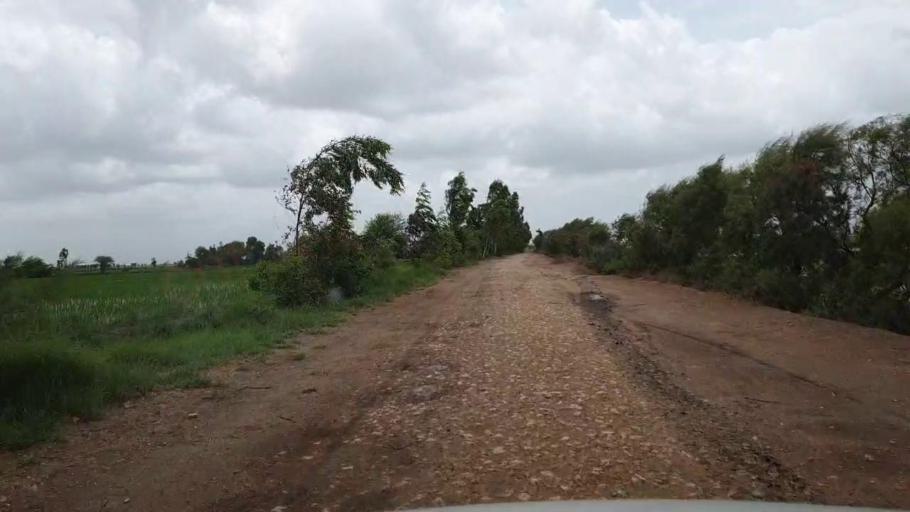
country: PK
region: Sindh
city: Kario
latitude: 24.7417
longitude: 68.5181
